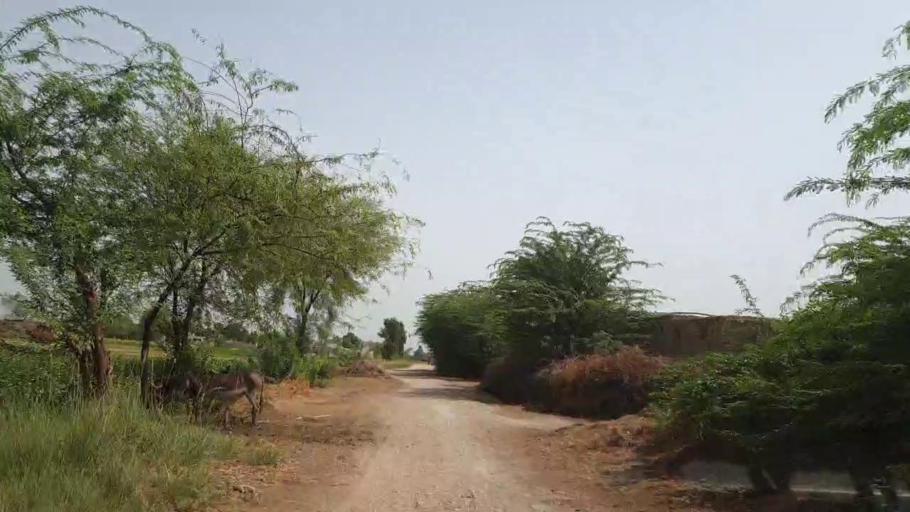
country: PK
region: Sindh
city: Sakrand
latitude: 26.1217
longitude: 68.3695
